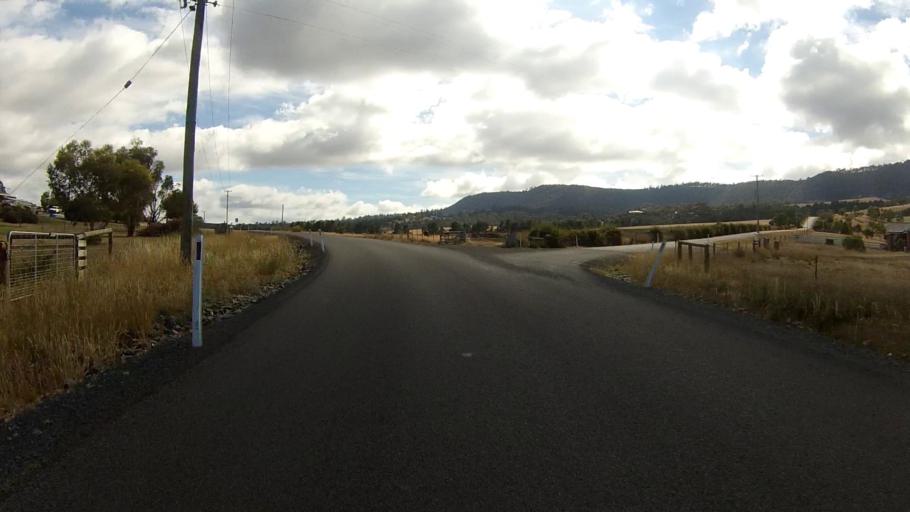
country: AU
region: Tasmania
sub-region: Brighton
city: Old Beach
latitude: -42.7666
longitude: 147.2989
